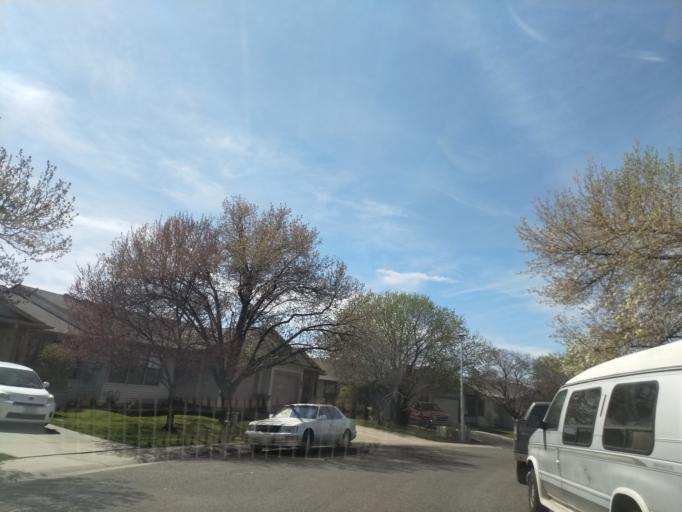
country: US
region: Colorado
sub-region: Mesa County
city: Grand Junction
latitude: 39.0799
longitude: -108.5304
